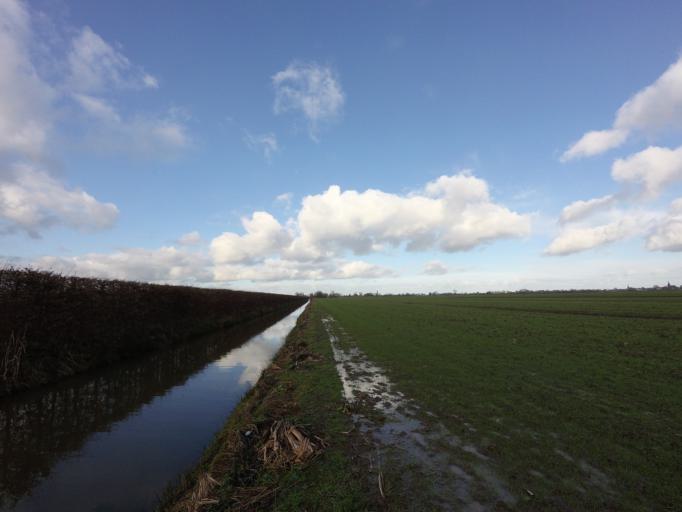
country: NL
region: Utrecht
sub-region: Gemeente Lopik
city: Lopik
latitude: 51.9938
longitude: 4.9632
